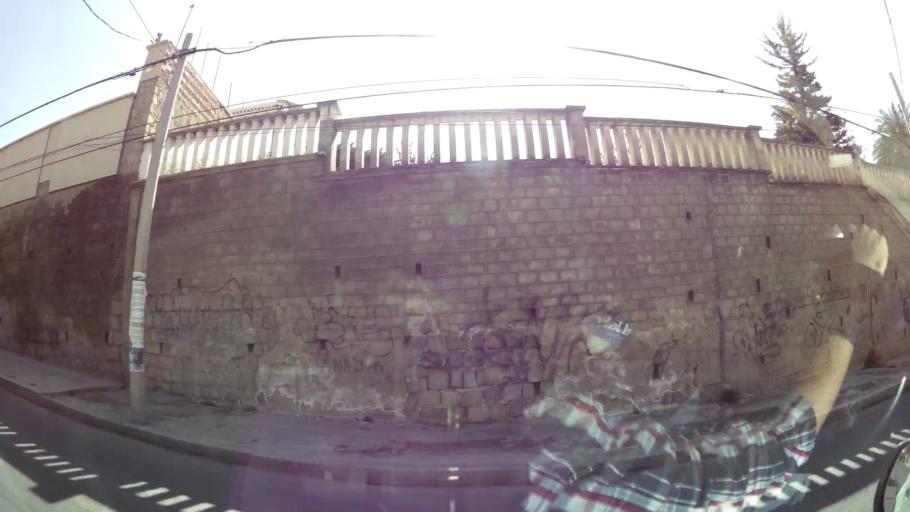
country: BO
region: La Paz
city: La Paz
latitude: -16.5246
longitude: -68.1096
